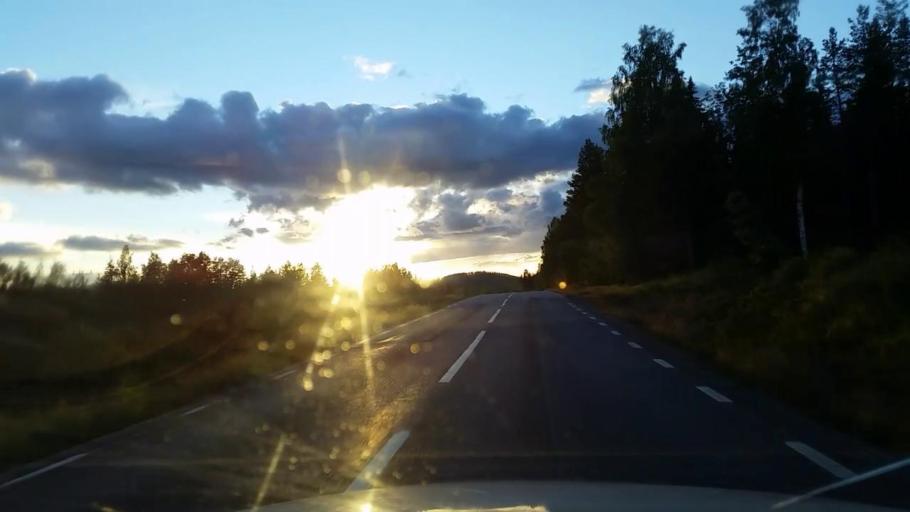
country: SE
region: Gaevleborg
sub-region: Ljusdals Kommun
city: Farila
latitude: 62.1334
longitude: 15.6959
